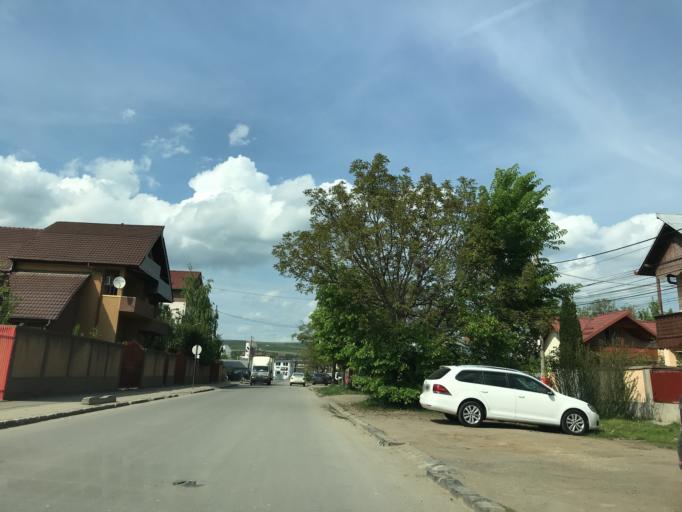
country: RO
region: Cluj
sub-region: Municipiul Cluj-Napoca
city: Cluj-Napoca
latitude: 46.7853
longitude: 23.6393
